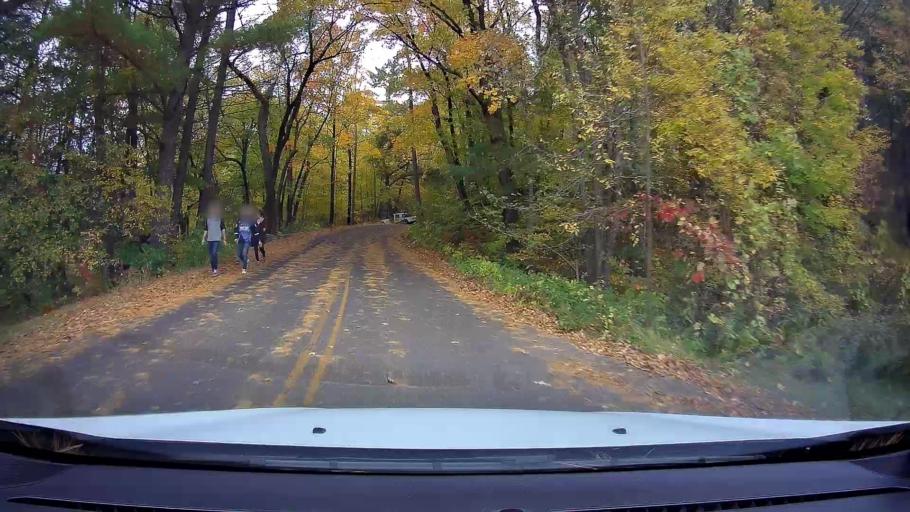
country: US
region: Wisconsin
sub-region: Polk County
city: Saint Croix Falls
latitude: 45.3941
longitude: -92.6501
